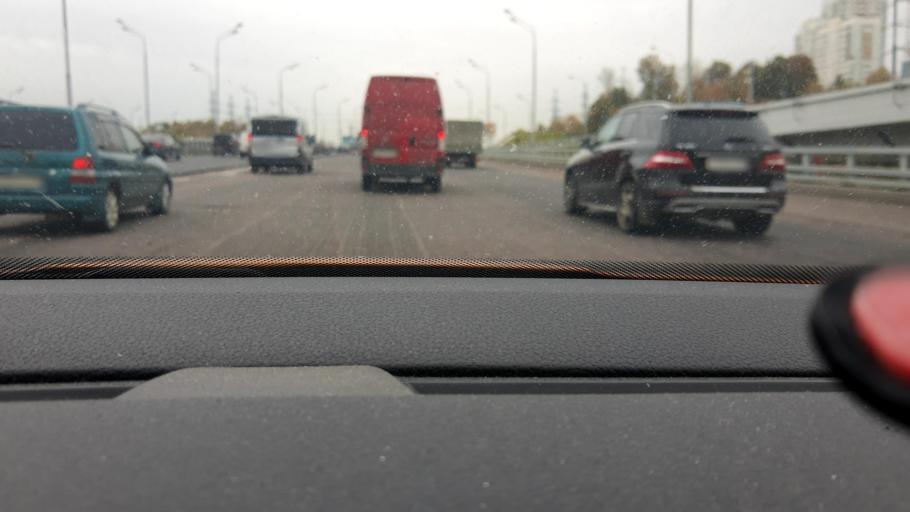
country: RU
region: Moscow
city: Strogino
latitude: 55.8459
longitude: 37.3945
